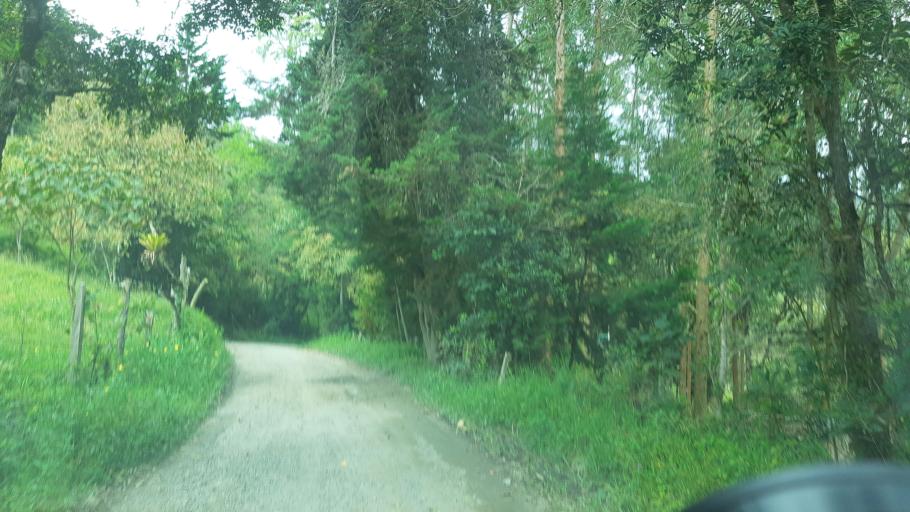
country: CO
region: Boyaca
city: Garagoa
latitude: 5.0486
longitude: -73.3521
